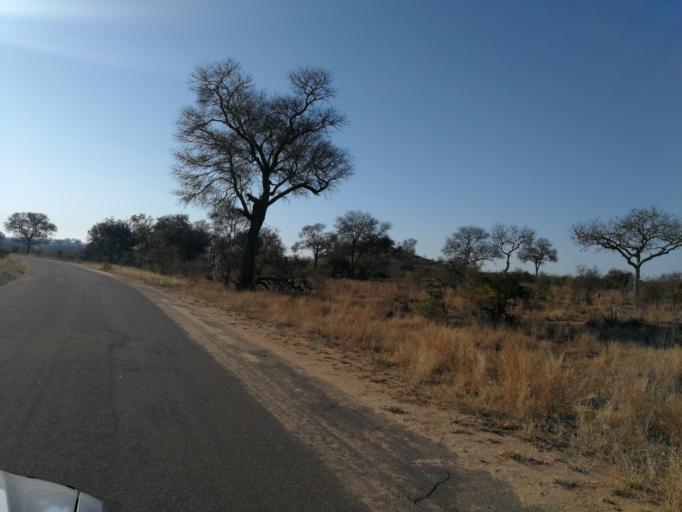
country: ZA
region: Limpopo
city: Thulamahashi
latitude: -25.0124
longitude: 31.4583
